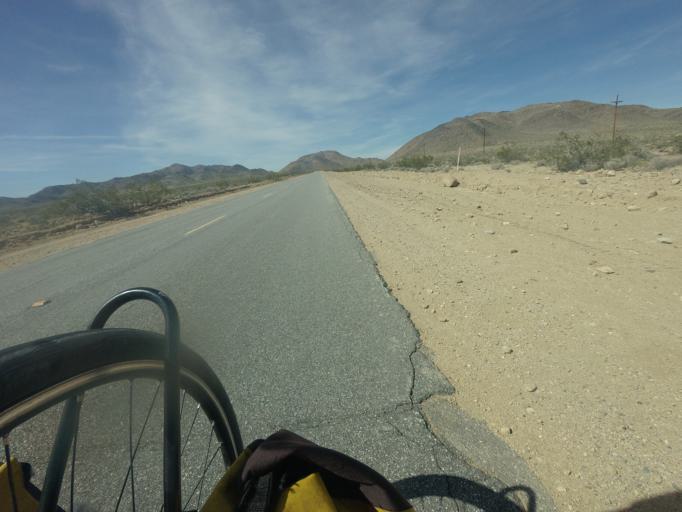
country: US
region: California
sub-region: San Bernardino County
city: Searles Valley
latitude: 35.5731
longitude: -117.4480
